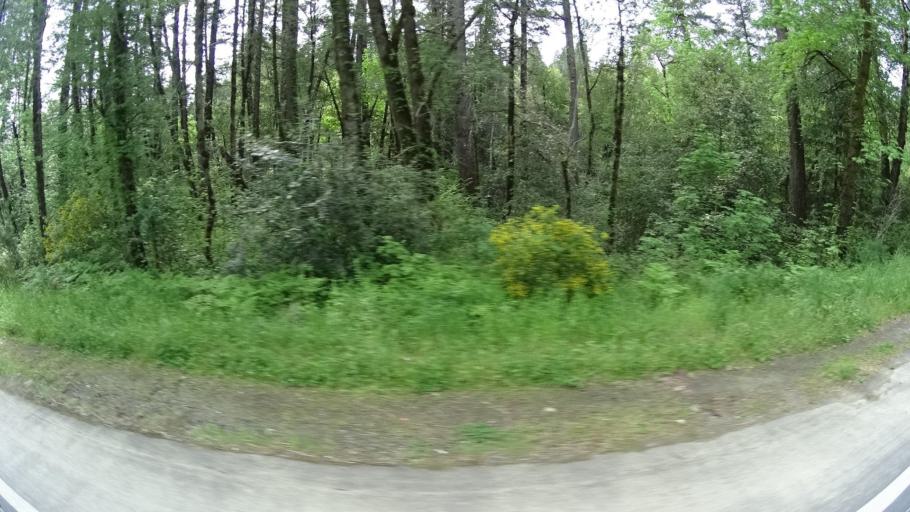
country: US
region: California
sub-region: Humboldt County
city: Redway
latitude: 40.1162
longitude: -123.8053
